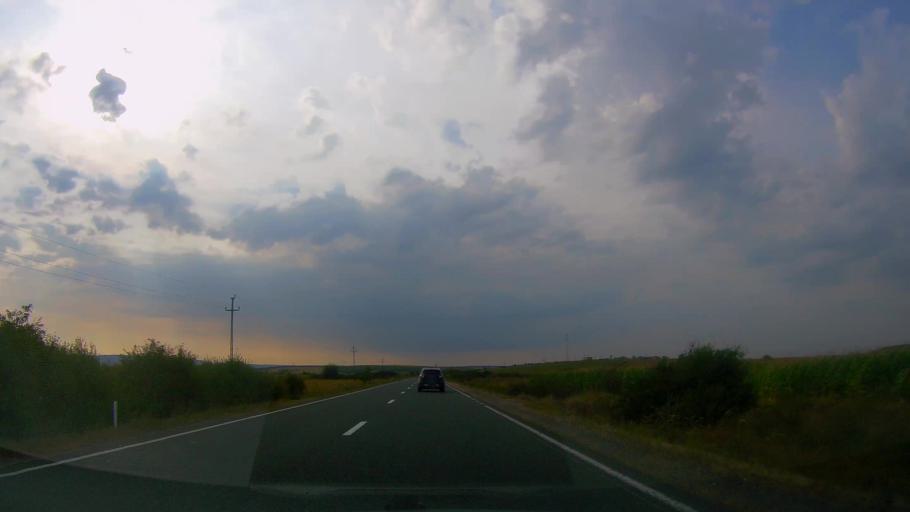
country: RO
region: Satu Mare
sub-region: Oras Ardud
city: Ardud
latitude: 47.6190
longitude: 22.8734
